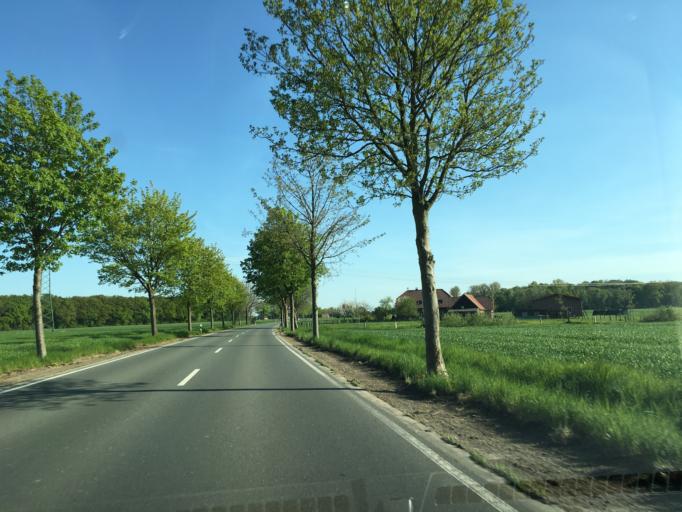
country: DE
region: North Rhine-Westphalia
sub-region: Regierungsbezirk Munster
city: Senden
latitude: 51.7984
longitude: 7.5377
